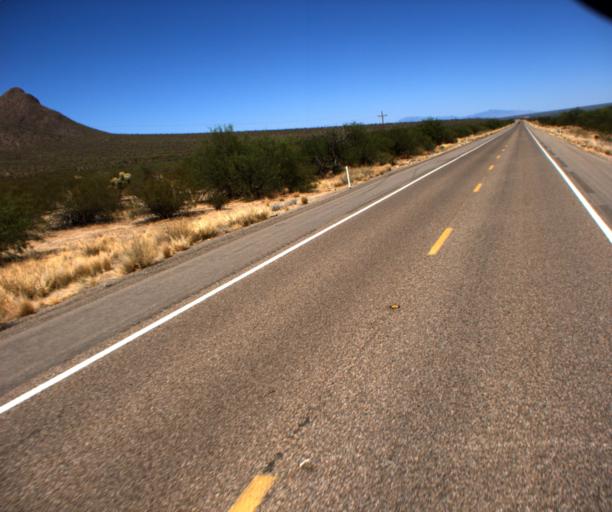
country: US
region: Arizona
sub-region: Pima County
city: Three Points
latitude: 32.0409
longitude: -111.4596
